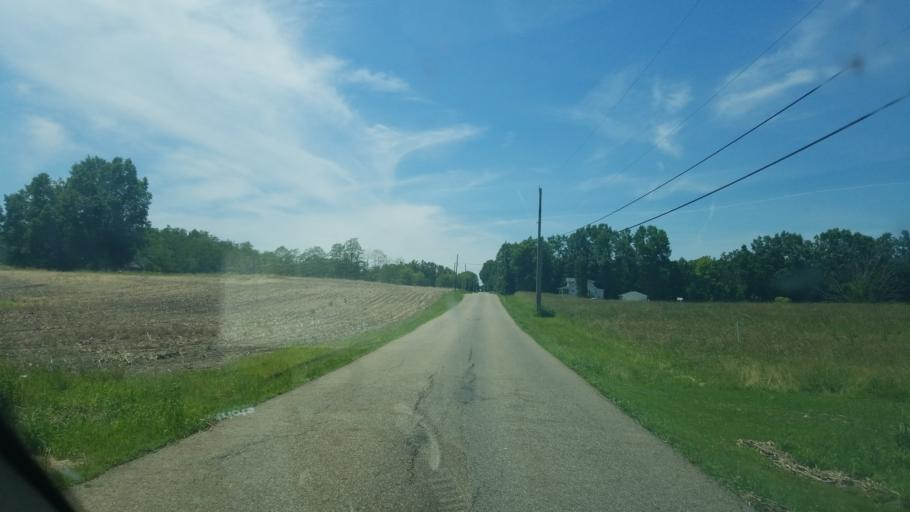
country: US
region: Ohio
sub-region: Stark County
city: Alliance
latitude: 40.8574
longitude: -81.0889
